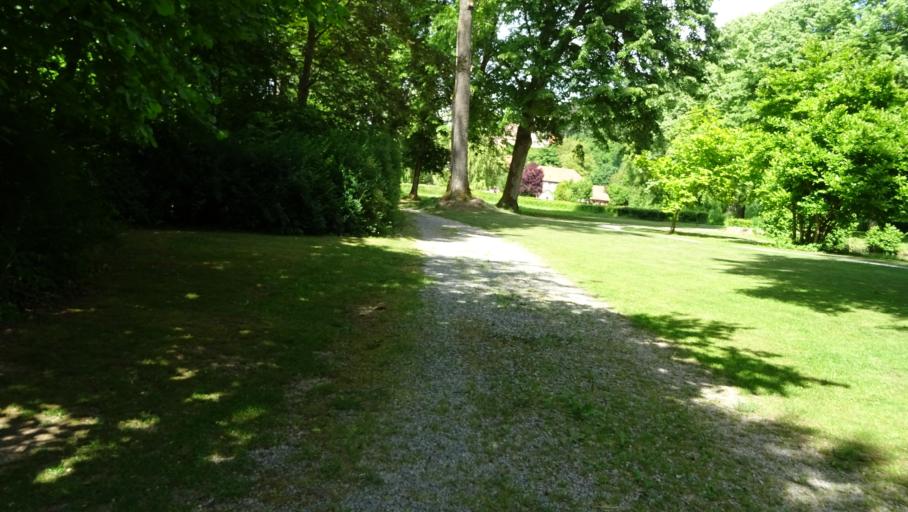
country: DE
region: Baden-Wuerttemberg
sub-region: Karlsruhe Region
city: Seckach
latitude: 49.4749
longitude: 9.3184
